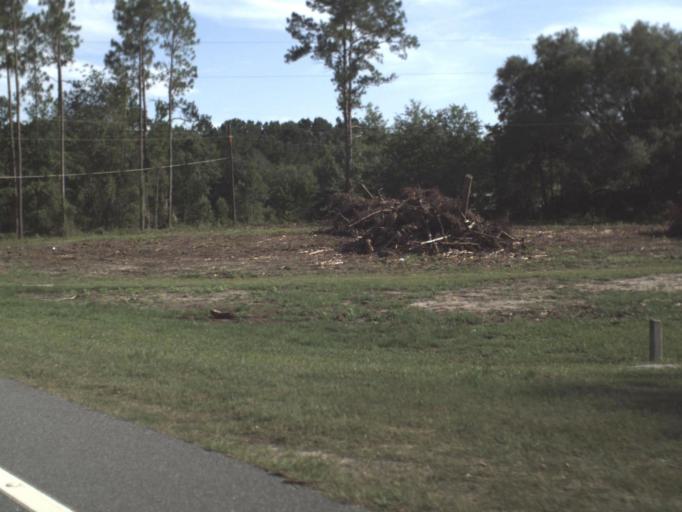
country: US
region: Florida
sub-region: Madison County
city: Madison
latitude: 30.4193
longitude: -83.3769
